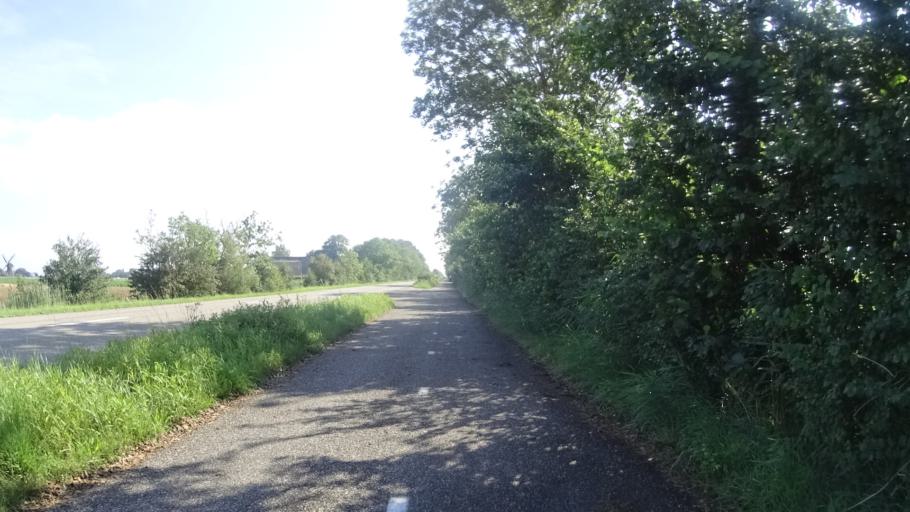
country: NL
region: Friesland
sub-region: Gemeente Franekeradeel
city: Tzum
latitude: 53.1917
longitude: 5.5872
